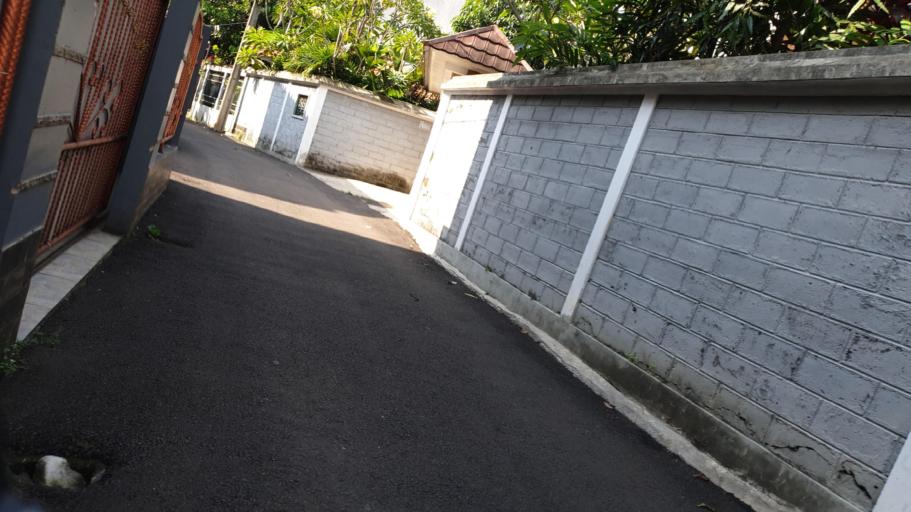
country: ID
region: West Java
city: Depok
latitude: -6.3279
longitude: 106.8255
